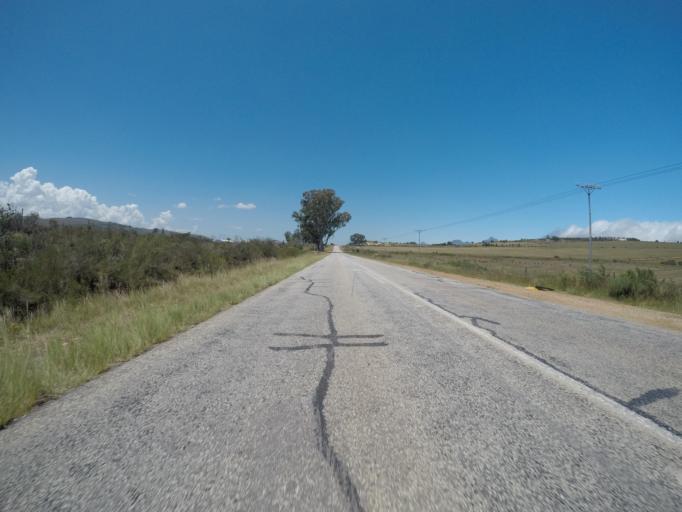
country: ZA
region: Western Cape
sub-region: Eden District Municipality
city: Plettenberg Bay
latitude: -33.7710
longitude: 23.5749
